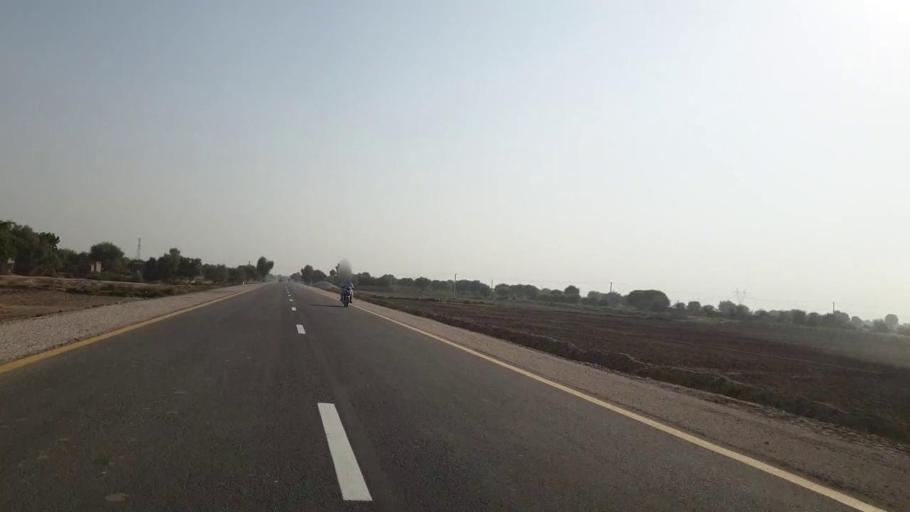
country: PK
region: Sindh
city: Bhan
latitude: 26.4907
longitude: 67.7798
